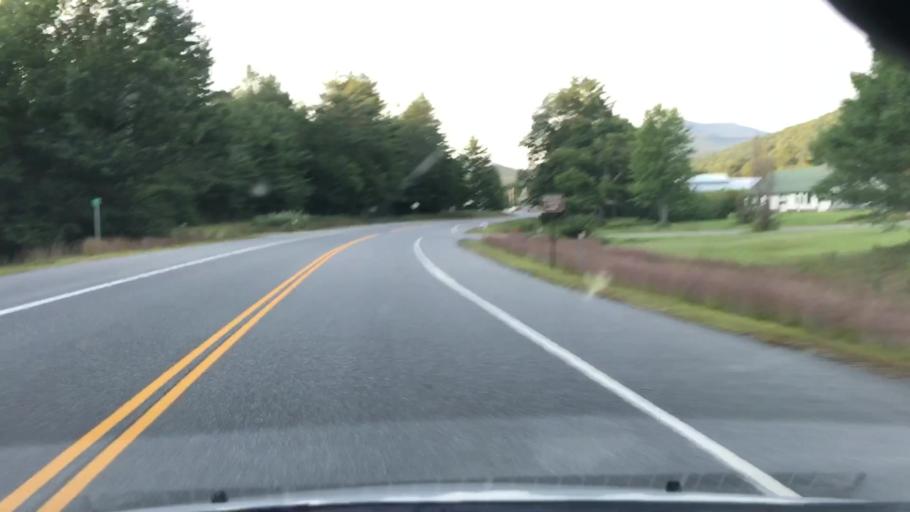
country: US
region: New Hampshire
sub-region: Grafton County
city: Rumney
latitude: 43.9095
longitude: -71.8889
